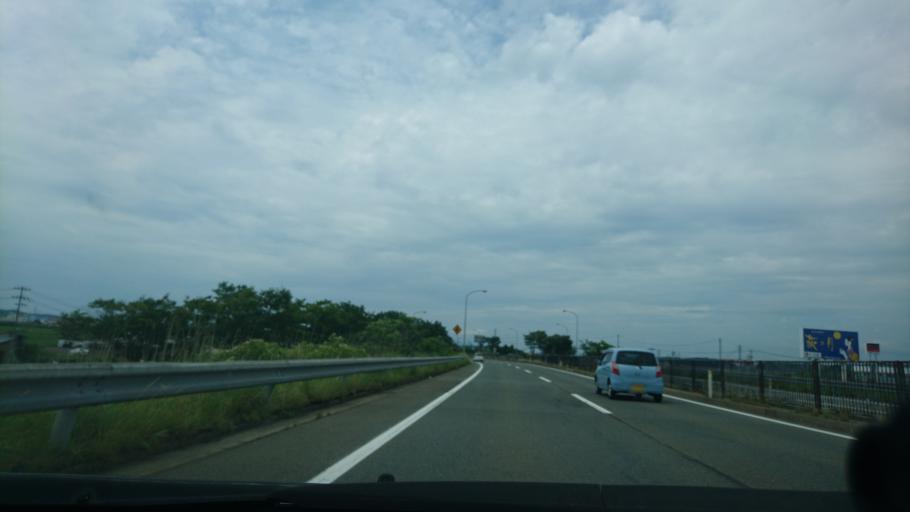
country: JP
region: Akita
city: Akita
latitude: 39.6754
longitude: 140.1511
